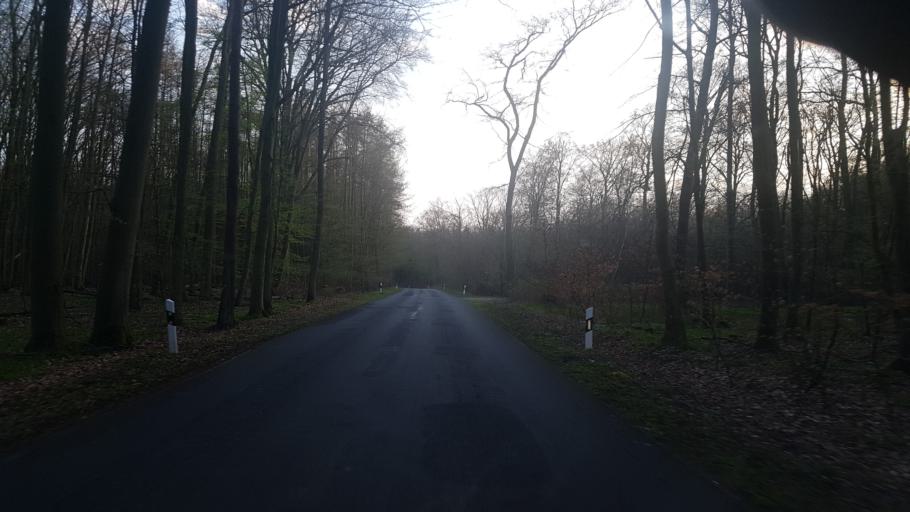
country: DE
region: Brandenburg
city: Gramzow
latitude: 53.1802
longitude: 13.9052
